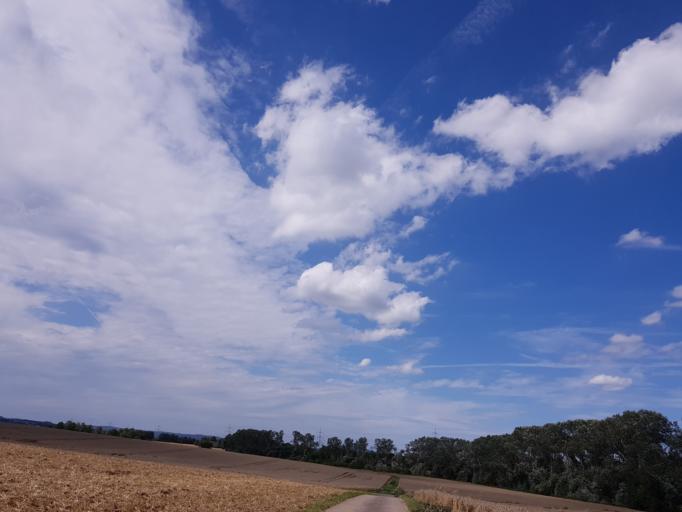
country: DE
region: Hesse
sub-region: Regierungsbezirk Giessen
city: Langgons
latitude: 50.5111
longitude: 8.6604
